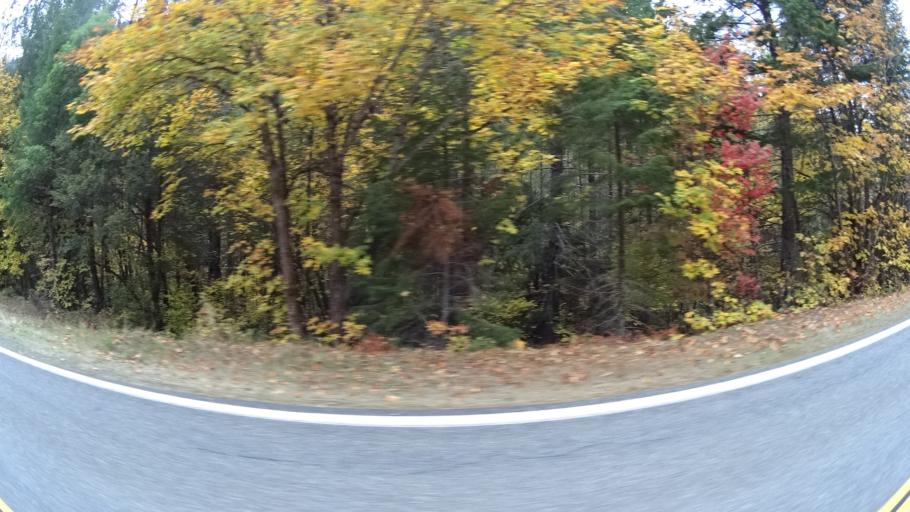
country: US
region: California
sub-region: Siskiyou County
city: Happy Camp
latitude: 41.9039
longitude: -123.4406
